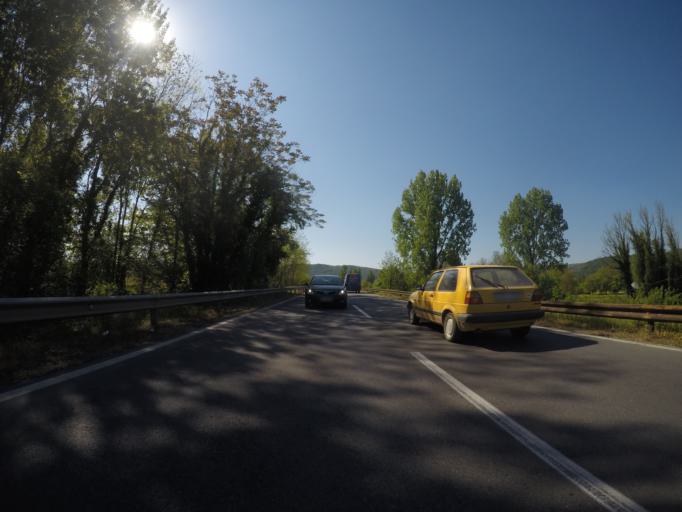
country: ME
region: Danilovgrad
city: Danilovgrad
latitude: 42.5208
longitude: 19.1210
